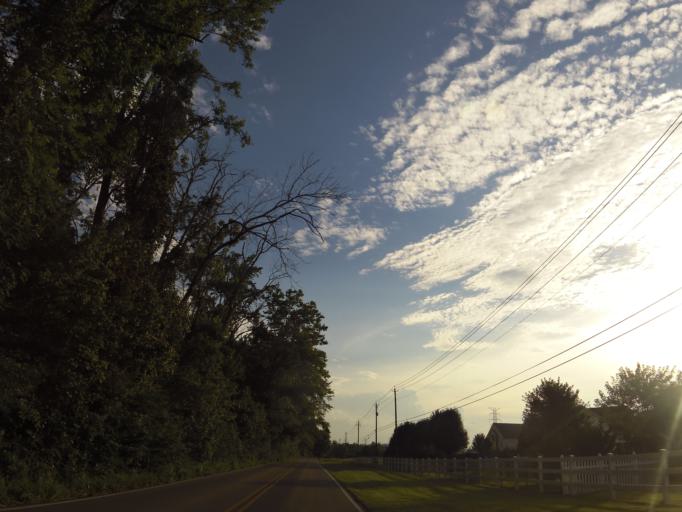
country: US
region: Tennessee
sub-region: Knox County
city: Knoxville
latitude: 36.0360
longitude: -83.9649
